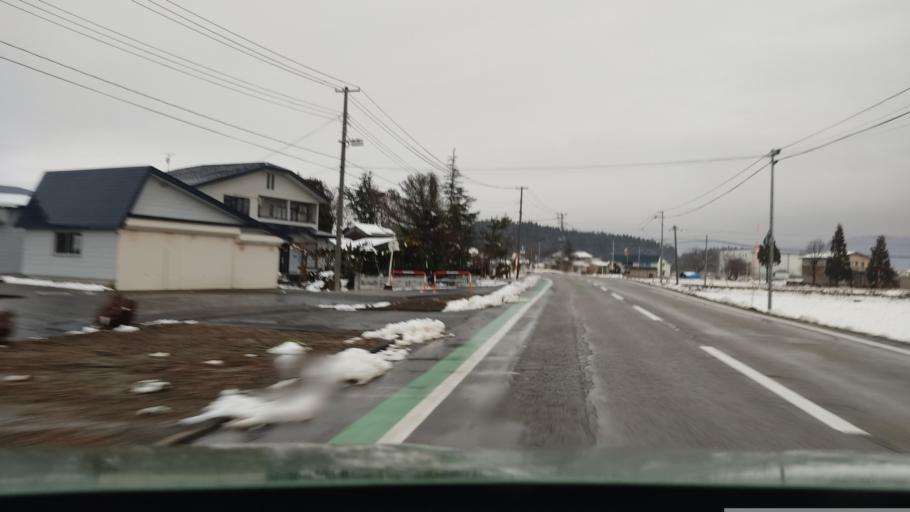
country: JP
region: Akita
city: Omagari
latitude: 39.4625
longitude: 140.5360
